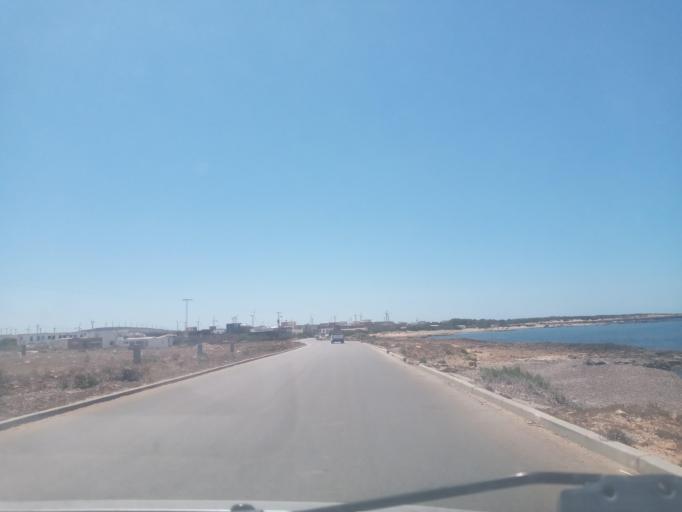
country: TN
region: Nabul
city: El Haouaria
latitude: 37.0496
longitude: 10.9750
